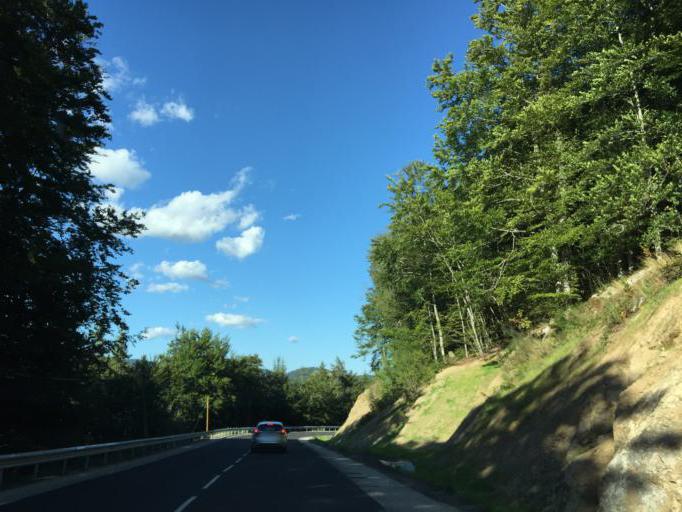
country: FR
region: Auvergne
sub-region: Departement de la Haute-Loire
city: Saugues
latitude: 44.9818
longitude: 3.6131
